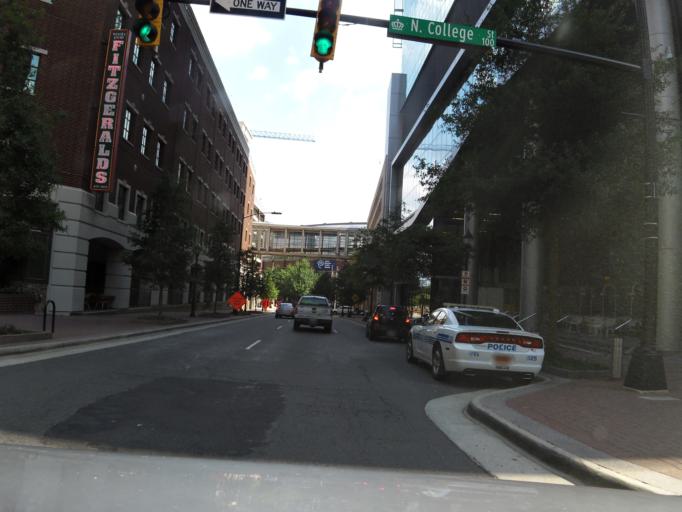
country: US
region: North Carolina
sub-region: Mecklenburg County
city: Charlotte
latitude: 35.2272
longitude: -80.8410
